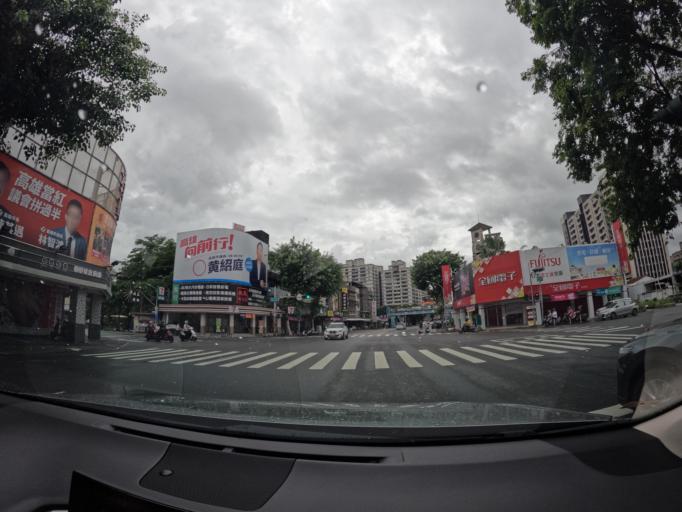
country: TW
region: Kaohsiung
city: Kaohsiung
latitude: 22.6330
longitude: 120.3279
